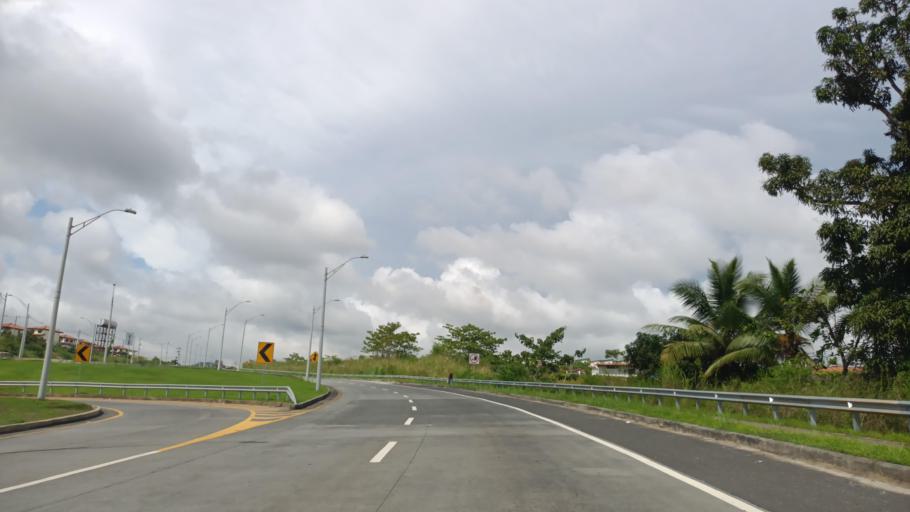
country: PA
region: Panama
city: Las Cumbres
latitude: 9.1014
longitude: -79.5169
